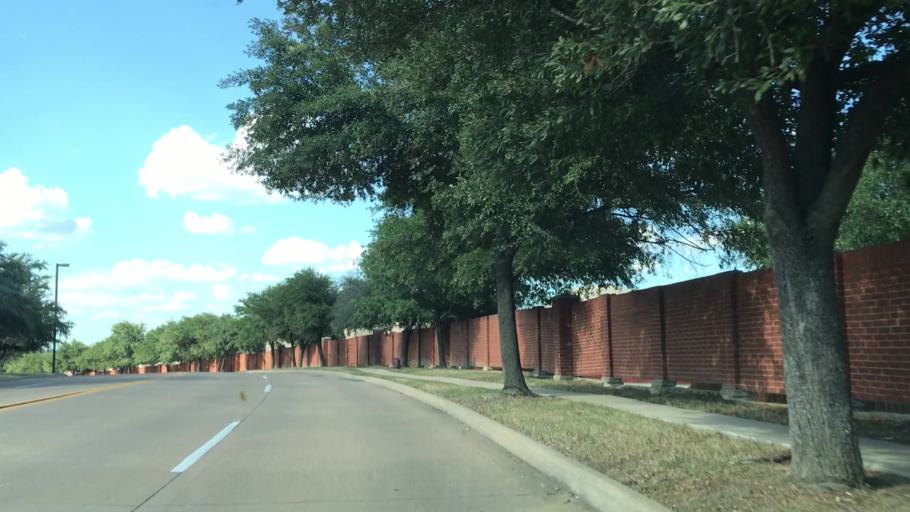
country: US
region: Texas
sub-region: Dallas County
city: Coppell
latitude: 32.9293
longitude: -96.9640
